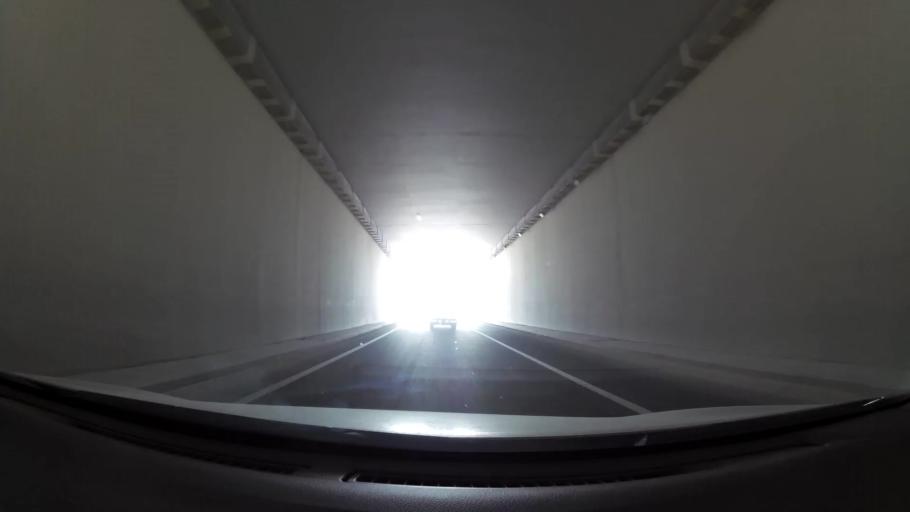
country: QA
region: Baladiyat Umm Salal
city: Umm Salal `Ali
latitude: 25.4820
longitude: 51.4062
